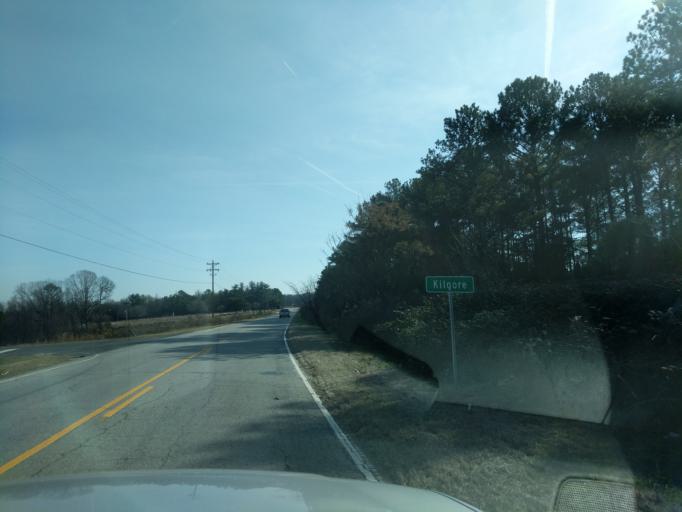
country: US
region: South Carolina
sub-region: Spartanburg County
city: Woodruff
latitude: 34.7053
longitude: -82.0117
